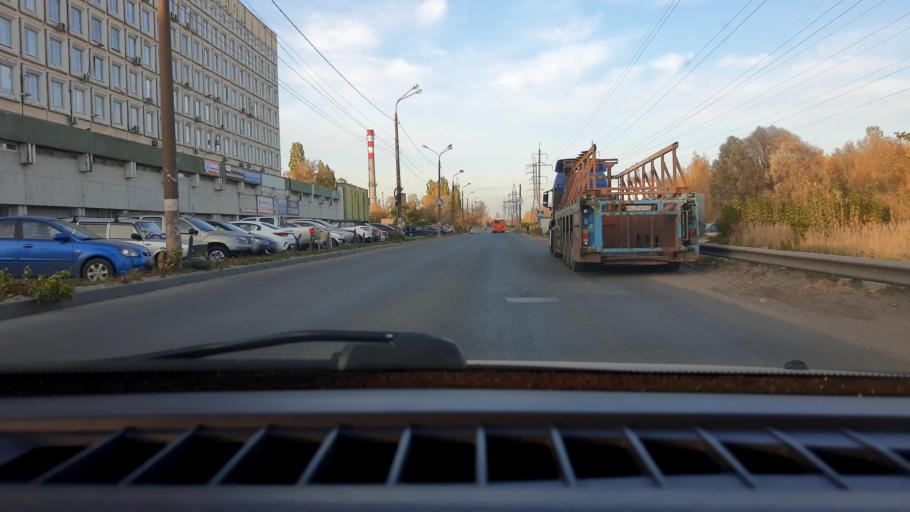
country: RU
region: Nizjnij Novgorod
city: Gorbatovka
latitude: 56.3659
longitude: 43.7952
